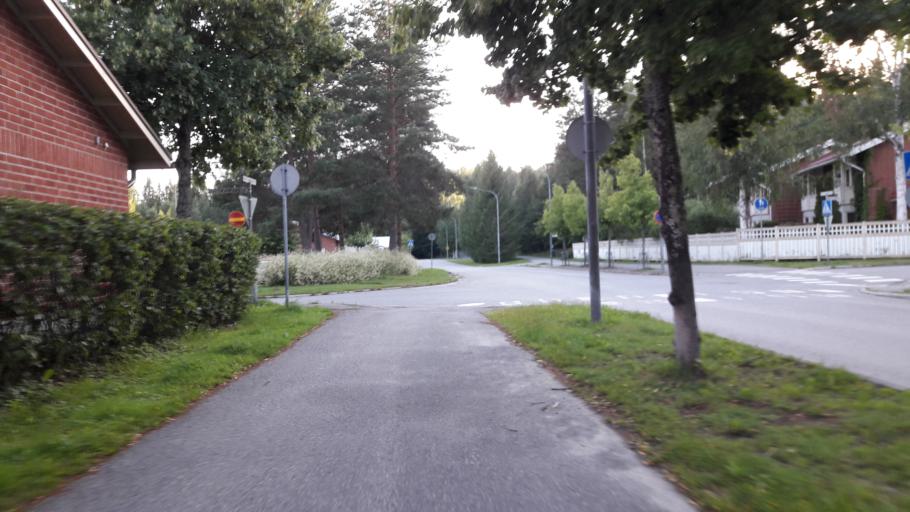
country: FI
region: North Karelia
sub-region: Joensuu
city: Joensuu
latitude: 62.6161
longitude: 29.7040
